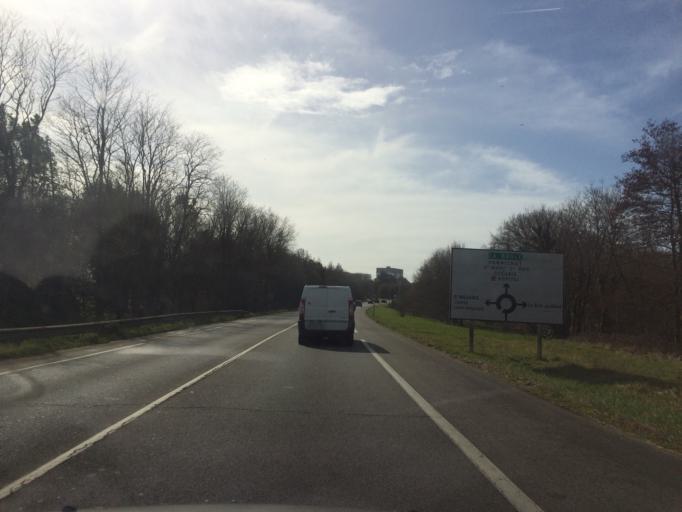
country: FR
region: Pays de la Loire
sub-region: Departement de la Loire-Atlantique
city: Saint-Nazaire
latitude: 47.2746
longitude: -2.2483
